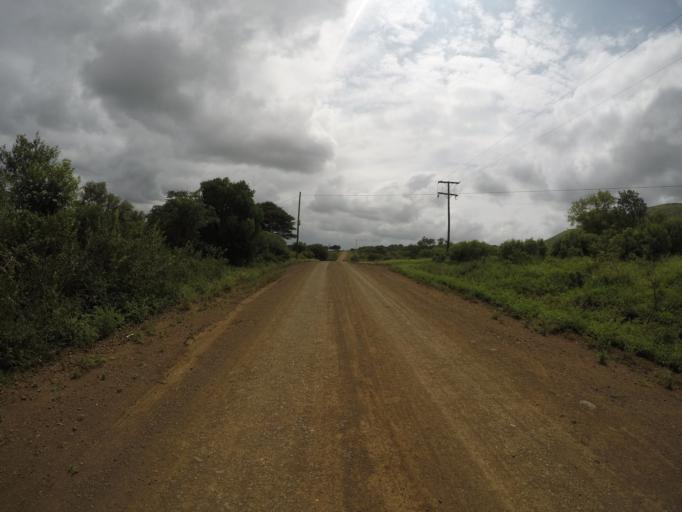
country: ZA
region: KwaZulu-Natal
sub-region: uThungulu District Municipality
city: Empangeni
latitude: -28.5742
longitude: 31.8717
